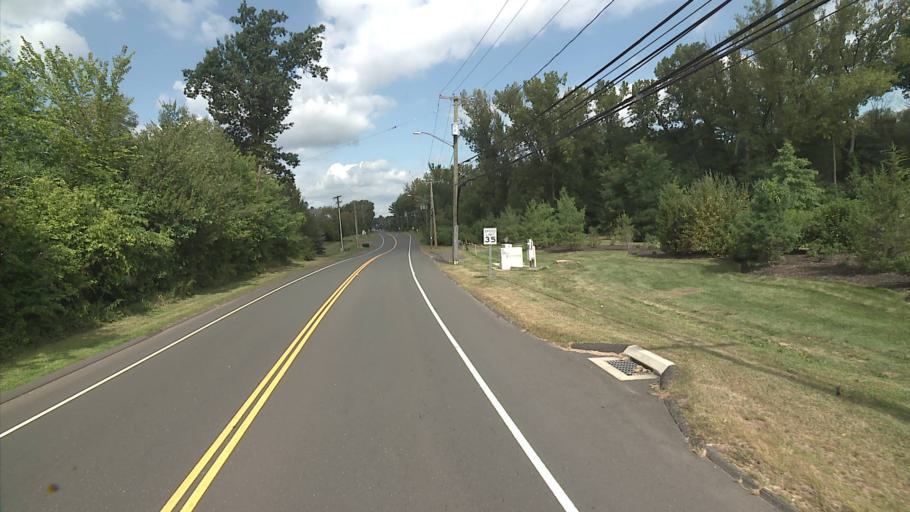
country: US
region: Connecticut
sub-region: Hartford County
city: Blue Hills
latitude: 41.7997
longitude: -72.7238
